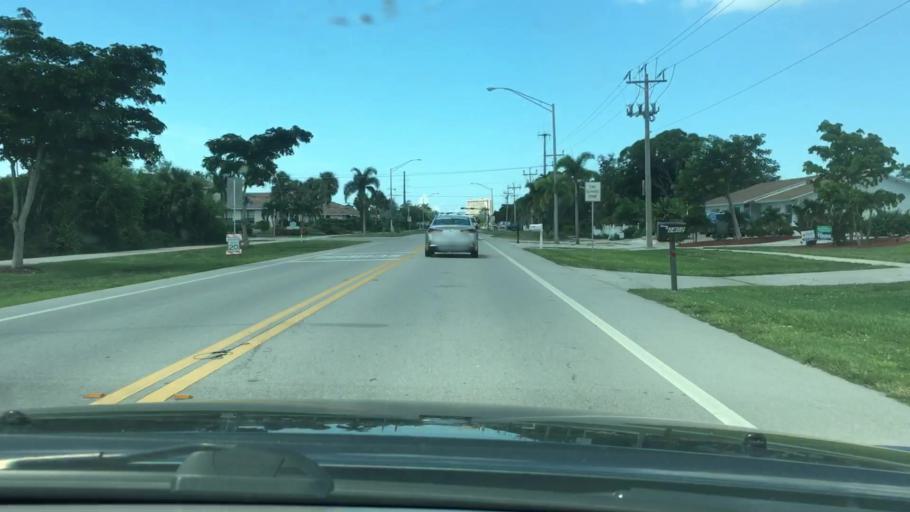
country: US
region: Florida
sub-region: Collier County
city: Marco
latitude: 25.9371
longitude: -81.7119
